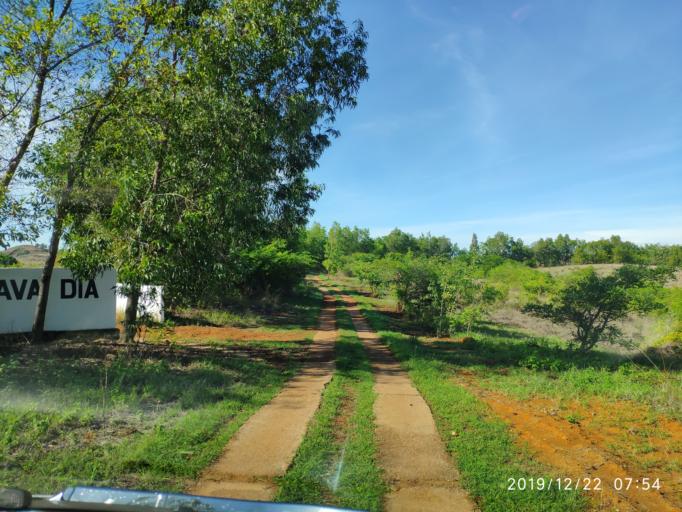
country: MG
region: Diana
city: Ambilobe
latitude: -12.9626
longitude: 49.1483
